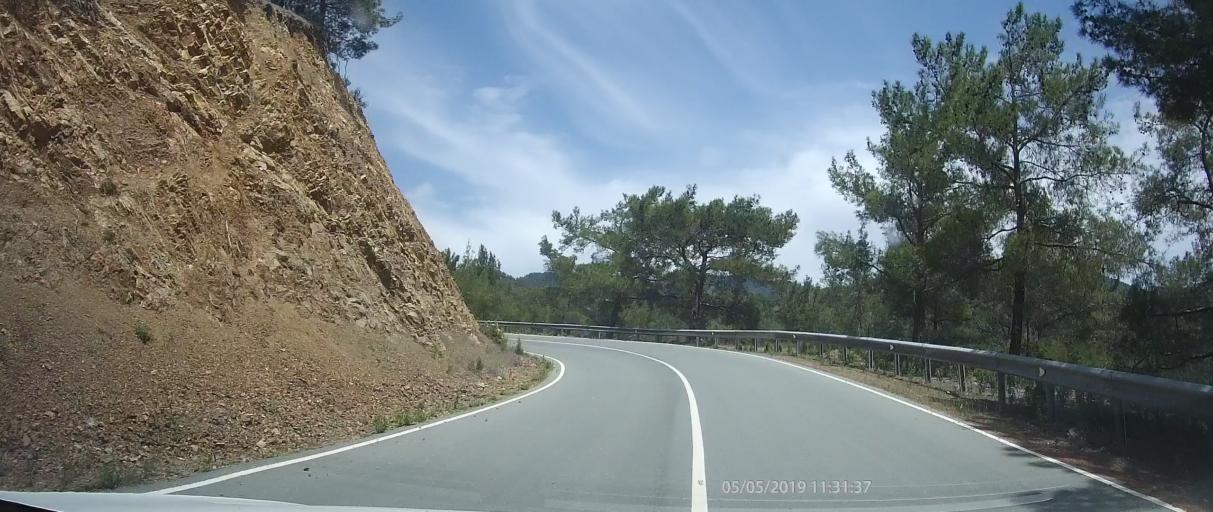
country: CY
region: Limassol
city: Pachna
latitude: 34.9506
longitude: 32.6468
